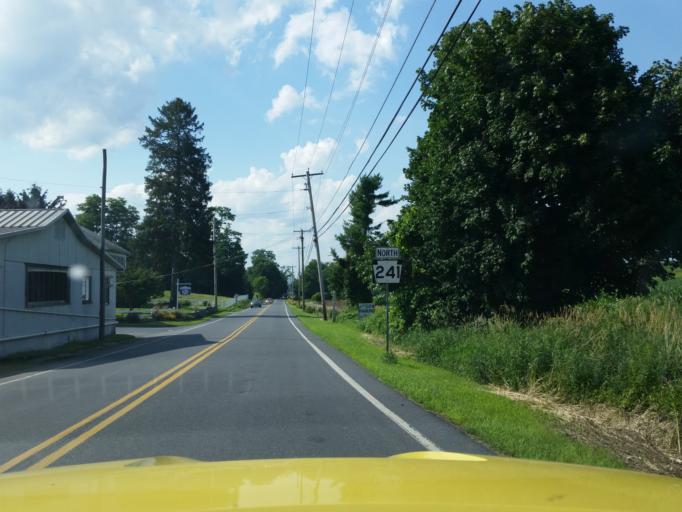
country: US
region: Pennsylvania
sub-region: Lebanon County
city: Cleona
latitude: 40.2713
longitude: -76.4831
